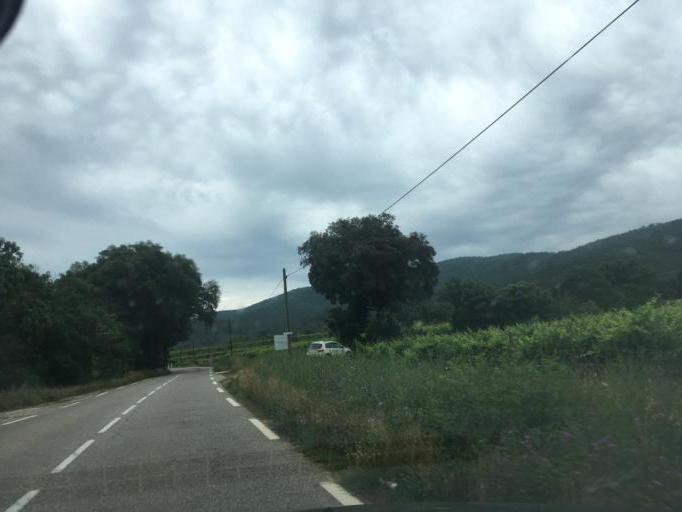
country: FR
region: Provence-Alpes-Cote d'Azur
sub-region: Departement du Var
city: Pierrefeu-du-Var
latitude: 43.2323
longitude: 6.1788
